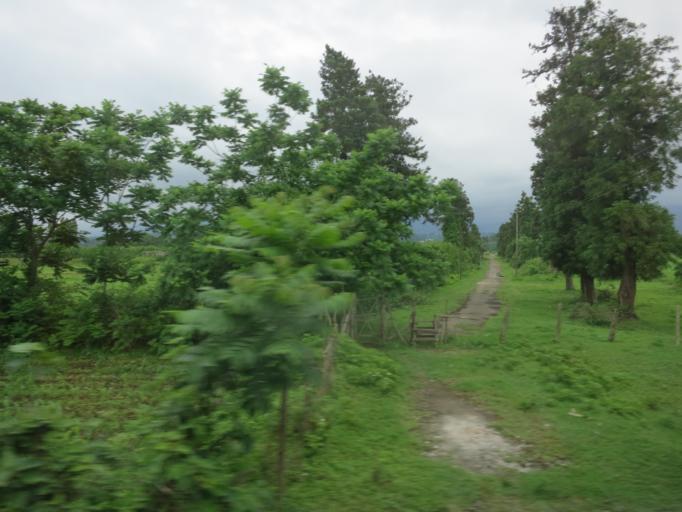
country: GE
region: Ajaria
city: Kobuleti
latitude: 41.7940
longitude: 41.7706
